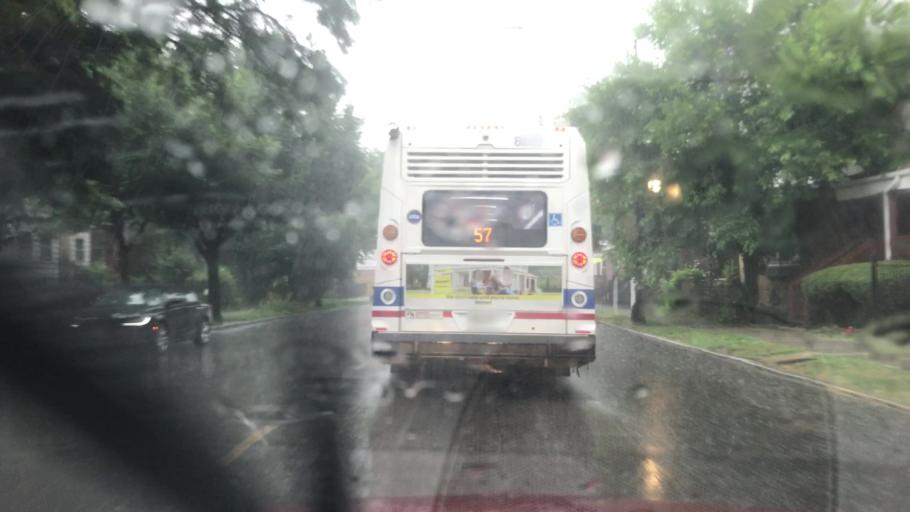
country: US
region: Illinois
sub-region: Cook County
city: Oak Park
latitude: 41.8831
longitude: -87.7551
